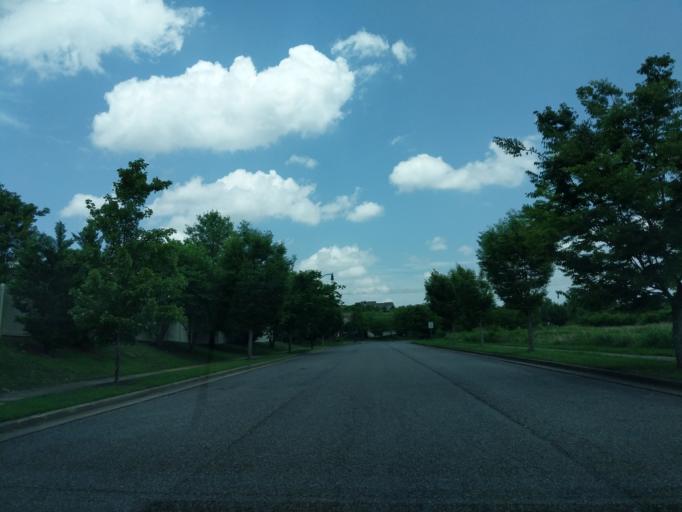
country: US
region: Tennessee
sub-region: Davidson County
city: Goodlettsville
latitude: 36.2994
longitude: -86.7262
